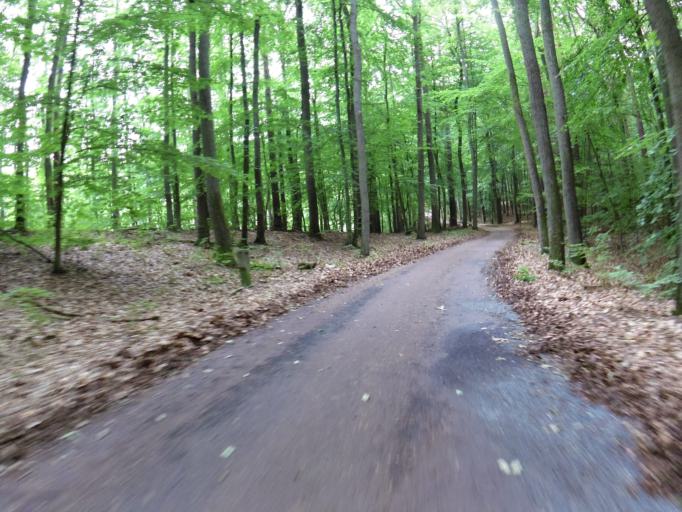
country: DE
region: Mecklenburg-Vorpommern
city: Seebad Heringsdorf
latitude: 53.9071
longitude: 14.1628
